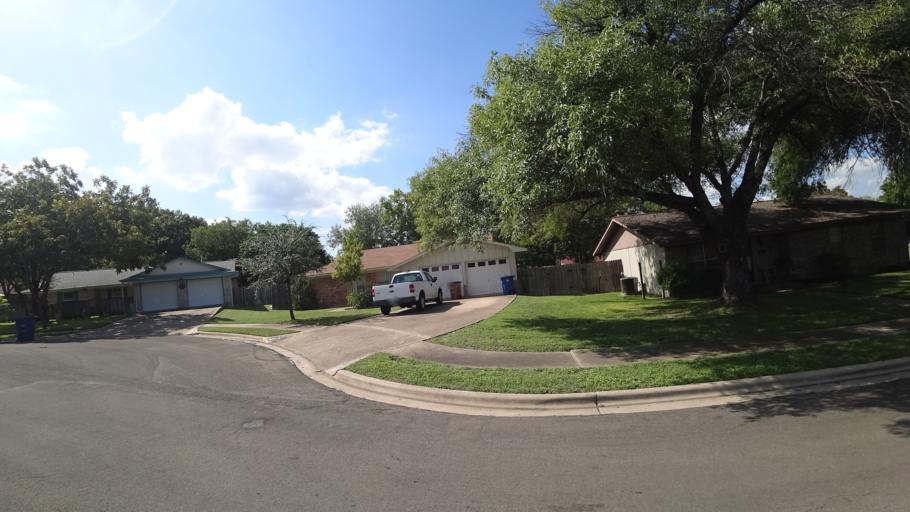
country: US
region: Texas
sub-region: Travis County
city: Wells Branch
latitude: 30.3657
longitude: -97.7108
